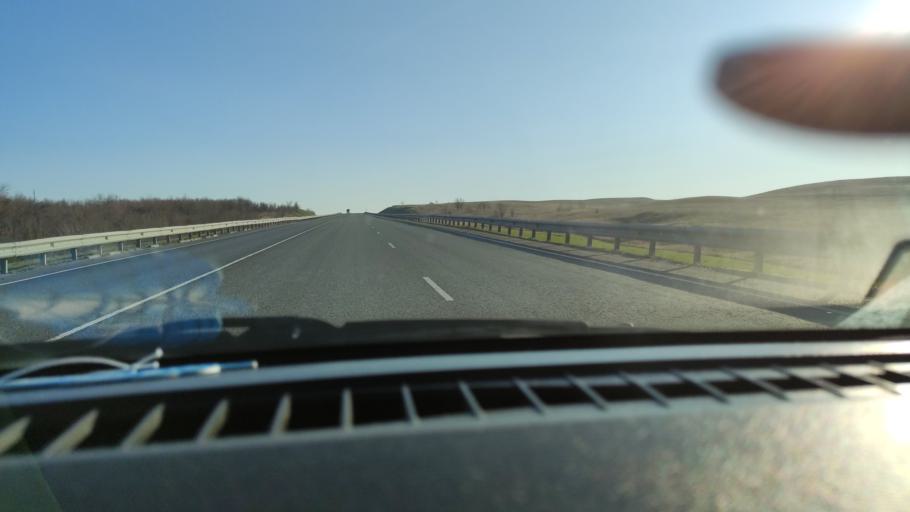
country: RU
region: Saratov
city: Alekseyevka
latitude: 52.2183
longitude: 47.8931
